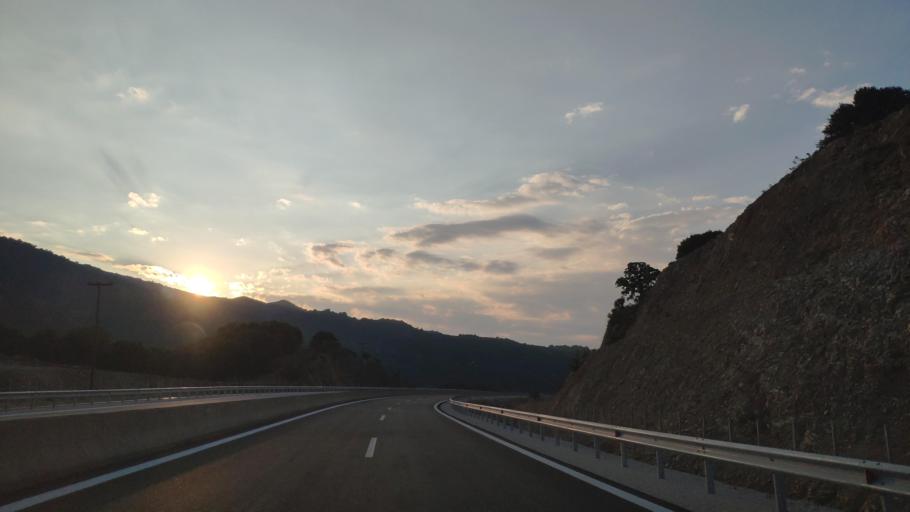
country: GR
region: West Greece
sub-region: Nomos Aitolias kai Akarnanias
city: Katouna
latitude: 38.8412
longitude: 21.1080
